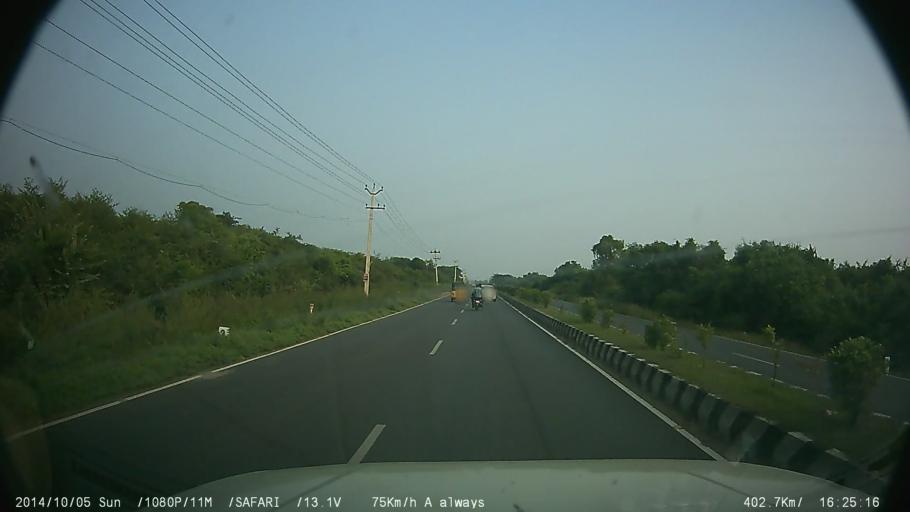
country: IN
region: Tamil Nadu
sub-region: Kancheepuram
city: Vengavasal
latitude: 12.8156
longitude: 80.1784
